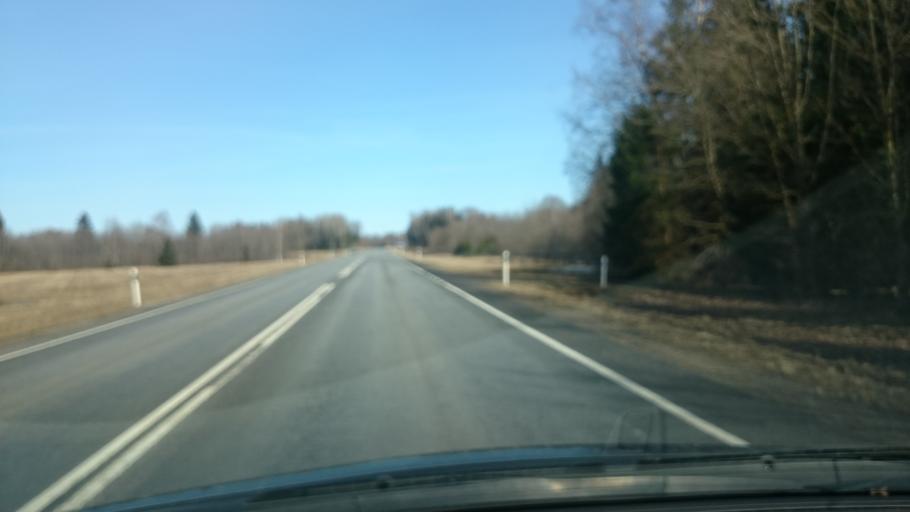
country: EE
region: Paernumaa
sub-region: Vaendra vald (alev)
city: Vandra
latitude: 58.6369
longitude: 24.9604
